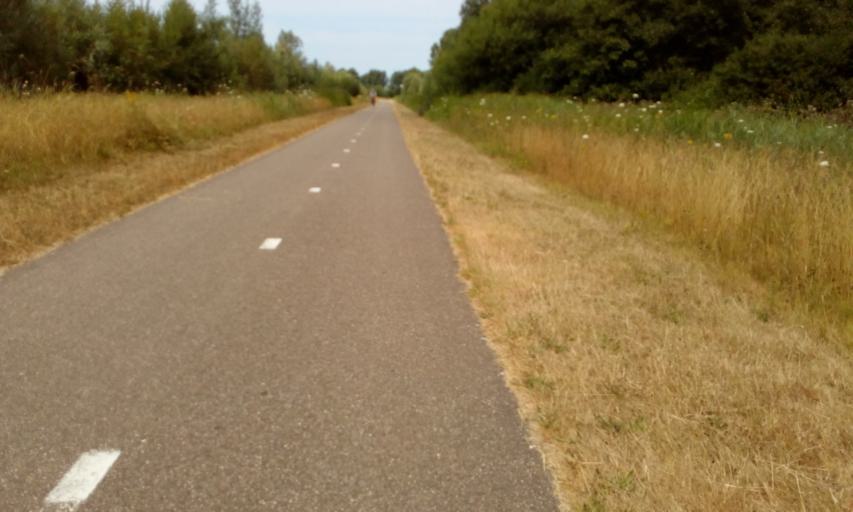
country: NL
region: South Holland
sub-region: Gemeente Pijnacker-Nootdorp
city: Pijnacker
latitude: 52.0470
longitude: 4.4343
